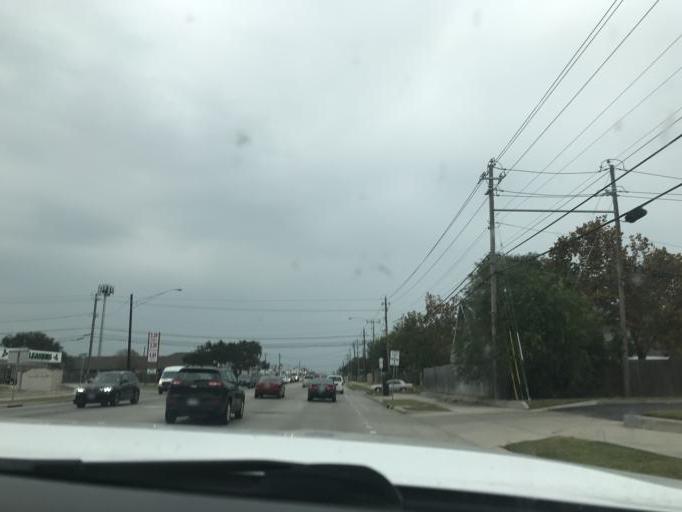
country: US
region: Texas
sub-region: Nueces County
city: Corpus Christi
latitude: 27.6992
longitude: -97.3752
